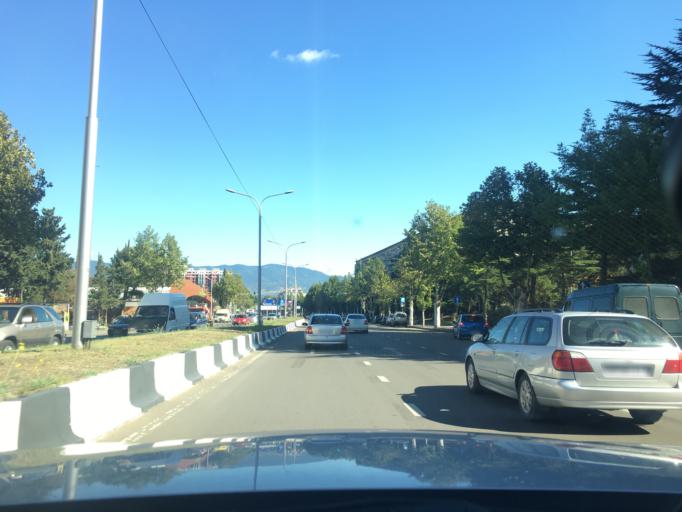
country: GE
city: Zahesi
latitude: 41.7668
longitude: 44.7907
